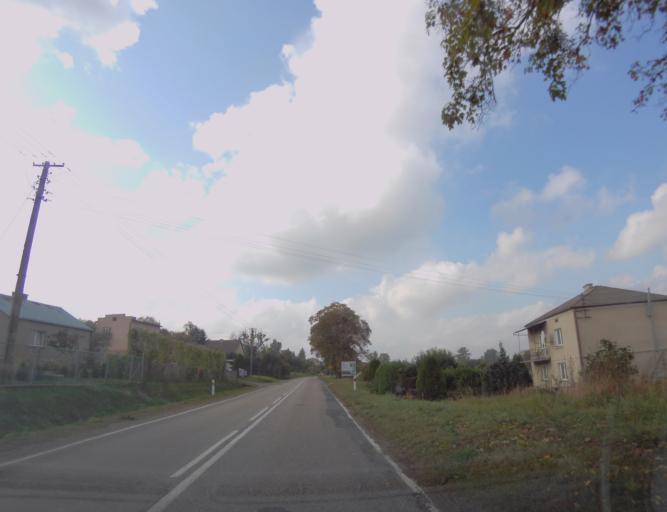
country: PL
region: Lublin Voivodeship
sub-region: Powiat krasnostawski
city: Krasnystaw
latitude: 50.9690
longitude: 23.1288
